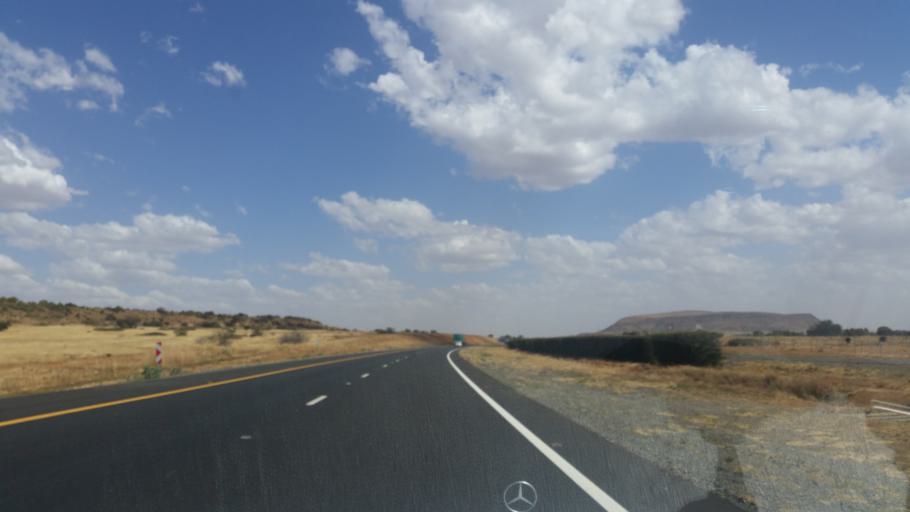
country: ZA
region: Orange Free State
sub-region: Mangaung Metropolitan Municipality
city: Bloemfontein
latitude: -29.1916
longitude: 26.1935
